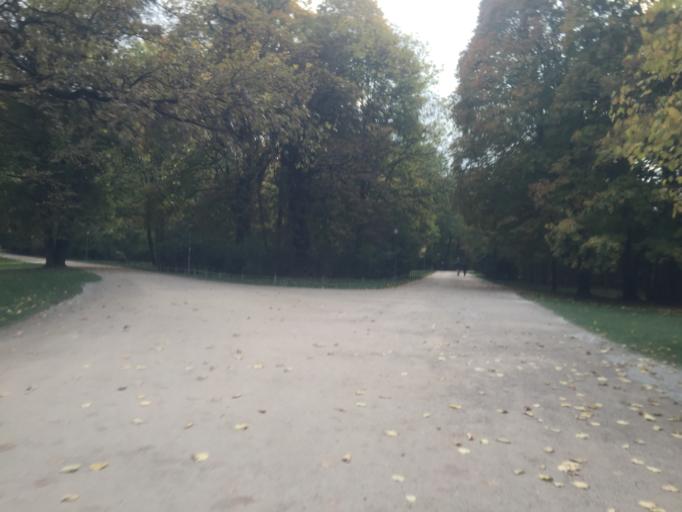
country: DE
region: Bavaria
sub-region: Upper Bavaria
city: Munich
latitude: 48.1482
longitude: 11.5908
